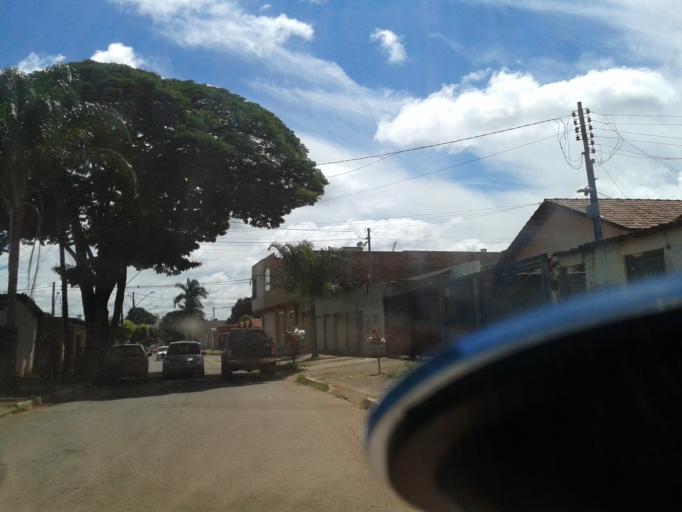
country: BR
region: Goias
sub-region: Goiania
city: Goiania
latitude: -16.6513
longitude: -49.3400
